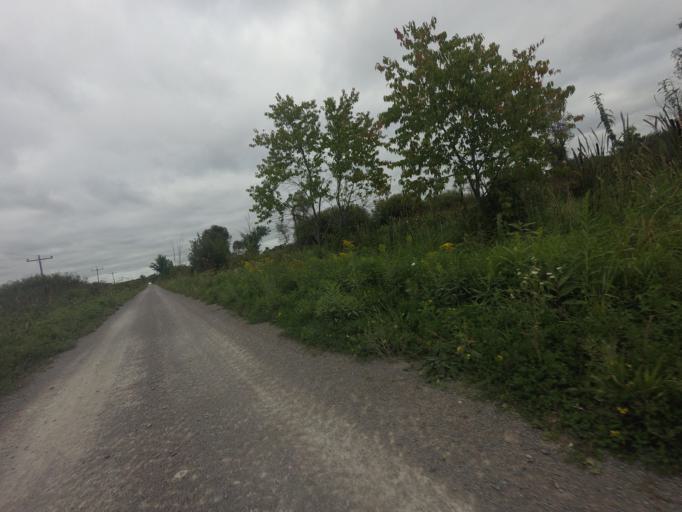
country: CA
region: Ontario
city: Omemee
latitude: 44.4763
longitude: -78.7474
